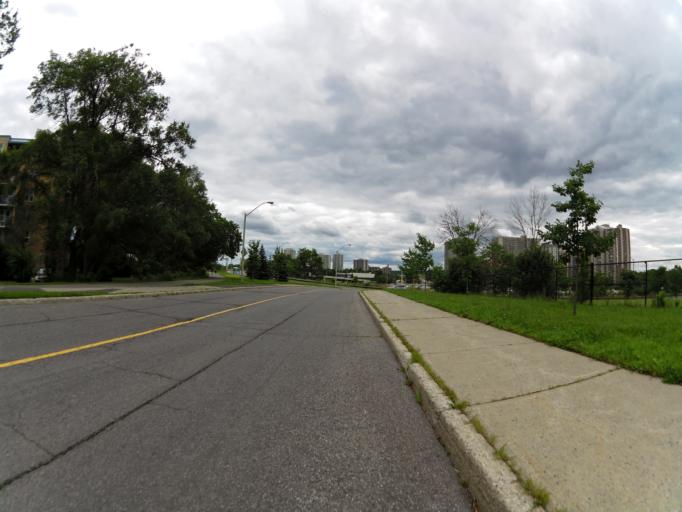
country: CA
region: Ontario
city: Ottawa
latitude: 45.4192
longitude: -75.6712
